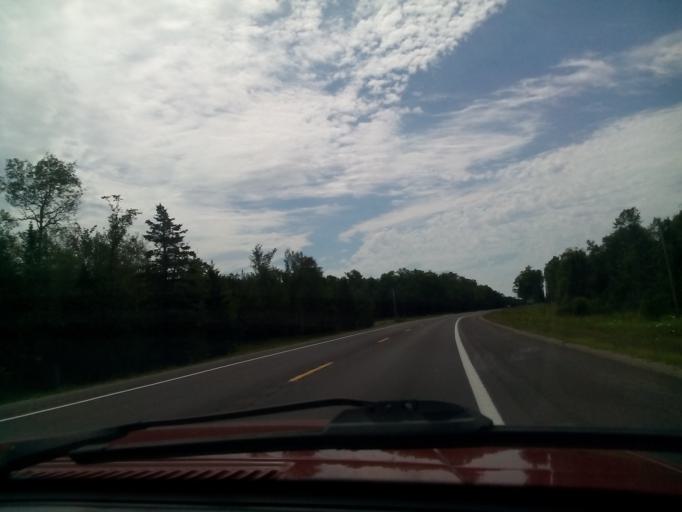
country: US
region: Michigan
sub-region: Schoolcraft County
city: Manistique
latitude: 46.0584
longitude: -85.9597
